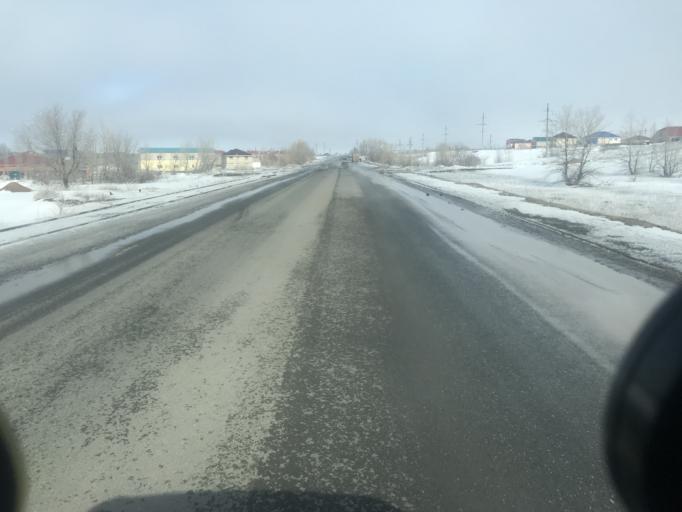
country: KZ
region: Aqtoebe
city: Aqtobe
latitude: 50.2831
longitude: 57.2833
